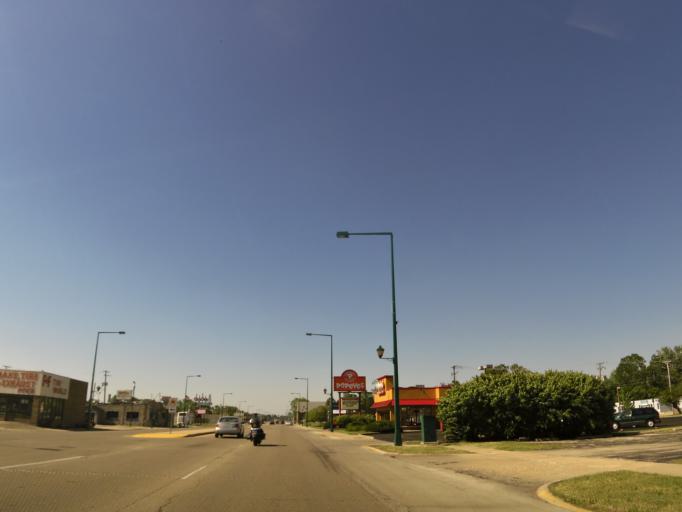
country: US
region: Illinois
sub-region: Winnebago County
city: Loves Park
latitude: 42.3067
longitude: -89.0577
